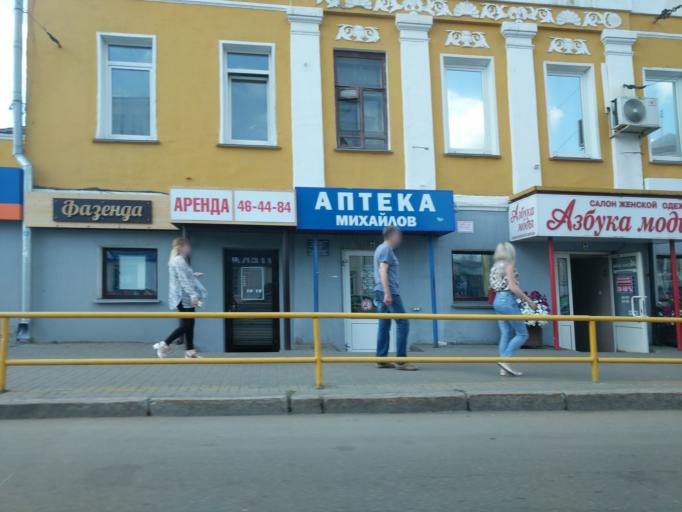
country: RU
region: Kirov
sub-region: Kirovo-Chepetskiy Rayon
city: Kirov
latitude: 58.6054
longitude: 49.6807
